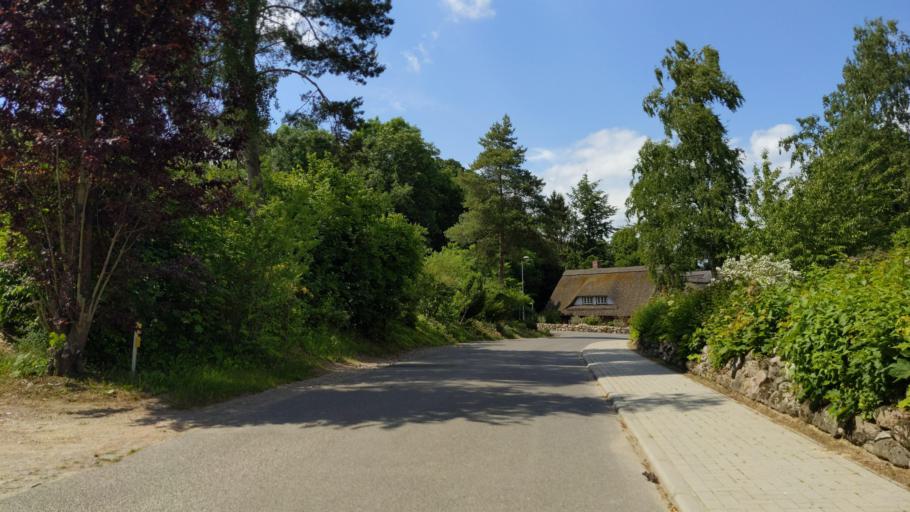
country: DE
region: Schleswig-Holstein
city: Kulpin
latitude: 53.7082
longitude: 10.6970
